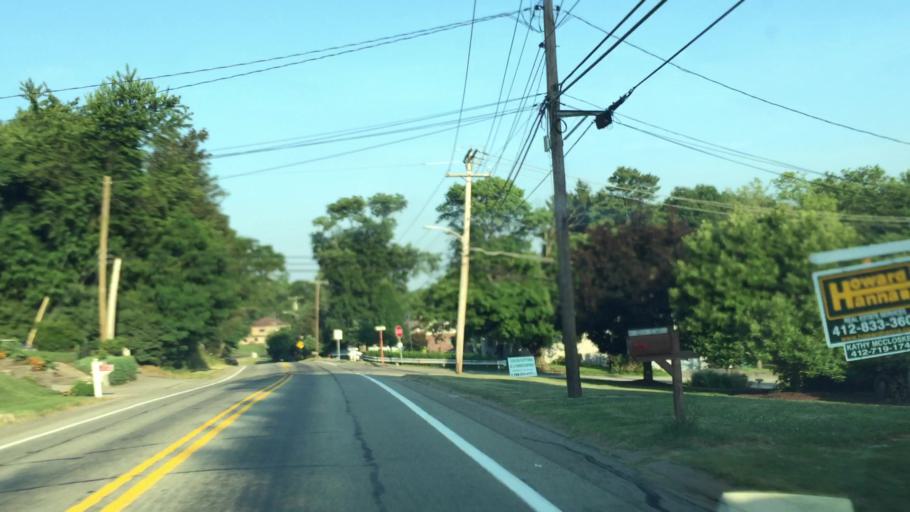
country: US
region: Pennsylvania
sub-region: Allegheny County
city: Bethel Park
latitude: 40.3001
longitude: -80.0504
